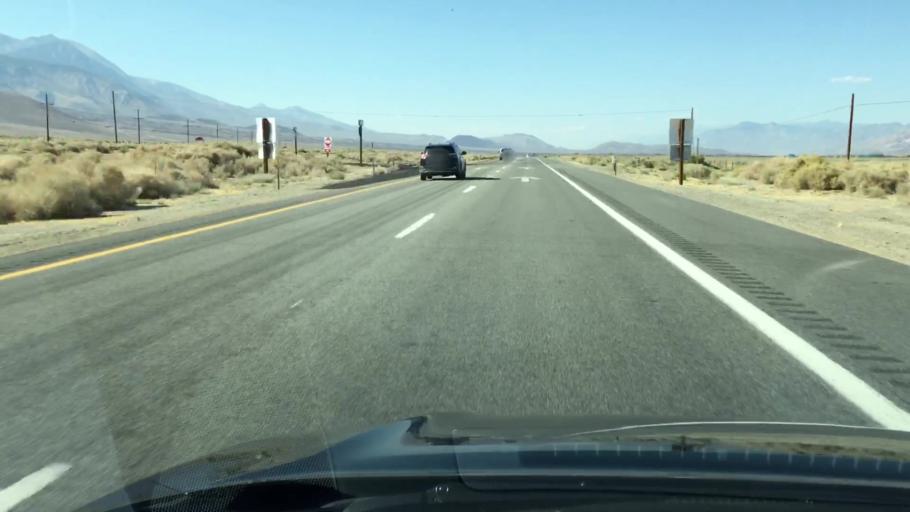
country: US
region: California
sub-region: Inyo County
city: Big Pine
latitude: 36.8748
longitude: -118.2379
